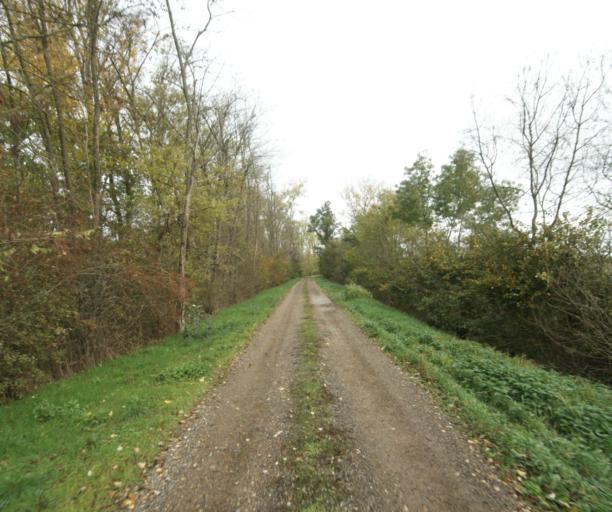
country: FR
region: Rhone-Alpes
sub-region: Departement de l'Ain
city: Pont-de-Vaux
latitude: 46.4589
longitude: 4.9021
